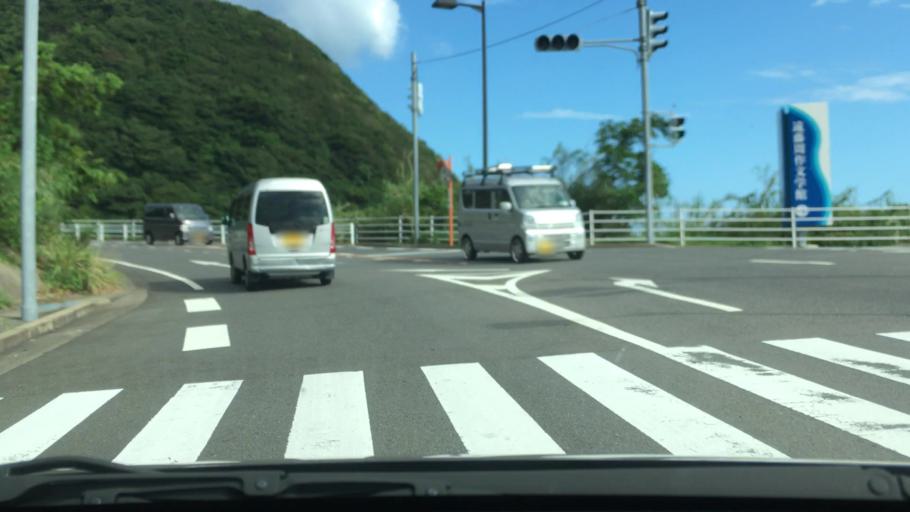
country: JP
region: Nagasaki
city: Togitsu
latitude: 32.8358
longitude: 129.7051
